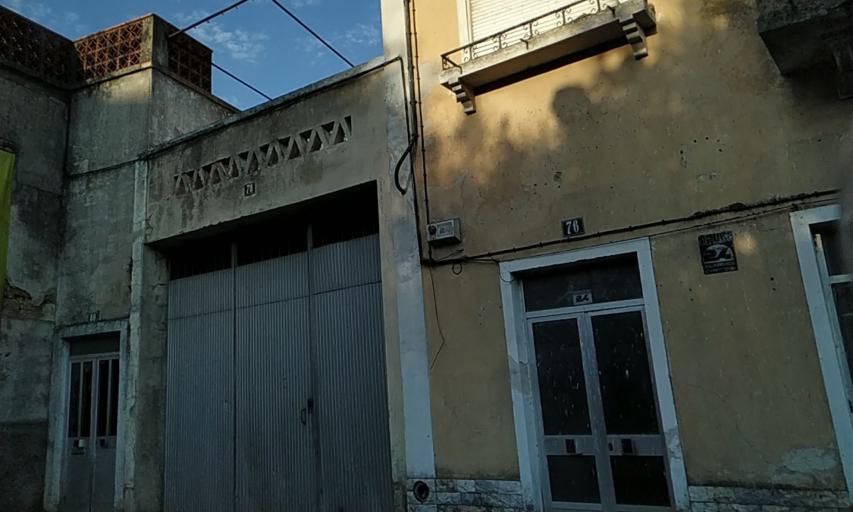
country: PT
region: Santarem
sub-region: Alcanena
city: Alcanena
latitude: 39.3825
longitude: -8.6600
